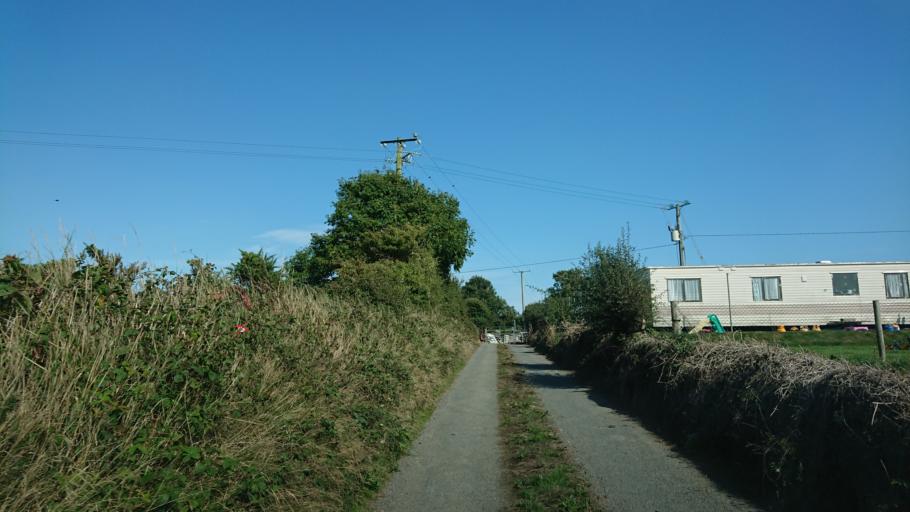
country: IE
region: Munster
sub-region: Waterford
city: Waterford
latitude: 52.2010
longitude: -7.0590
